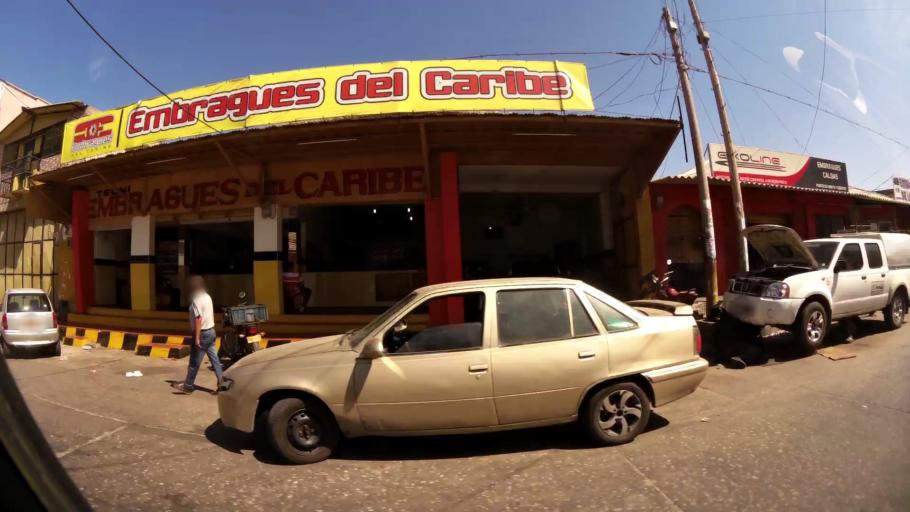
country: CO
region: Atlantico
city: Barranquilla
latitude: 10.9758
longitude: -74.7823
